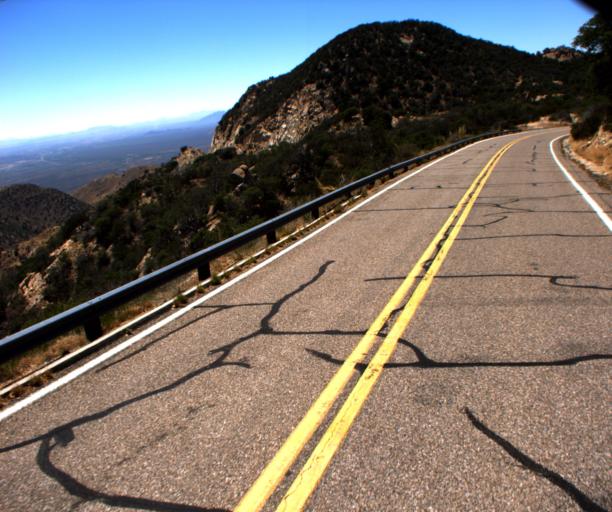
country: US
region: Arizona
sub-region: Pima County
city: Sells
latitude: 31.9499
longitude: -111.6193
